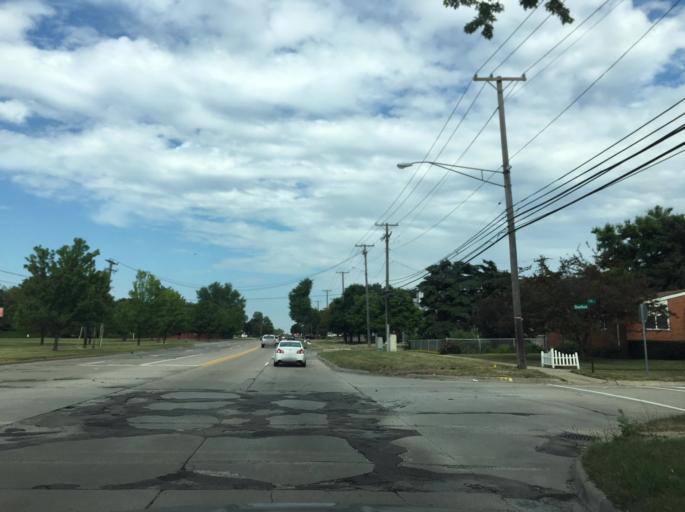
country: US
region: Michigan
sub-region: Macomb County
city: Sterling Heights
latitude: 42.5358
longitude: -83.0564
